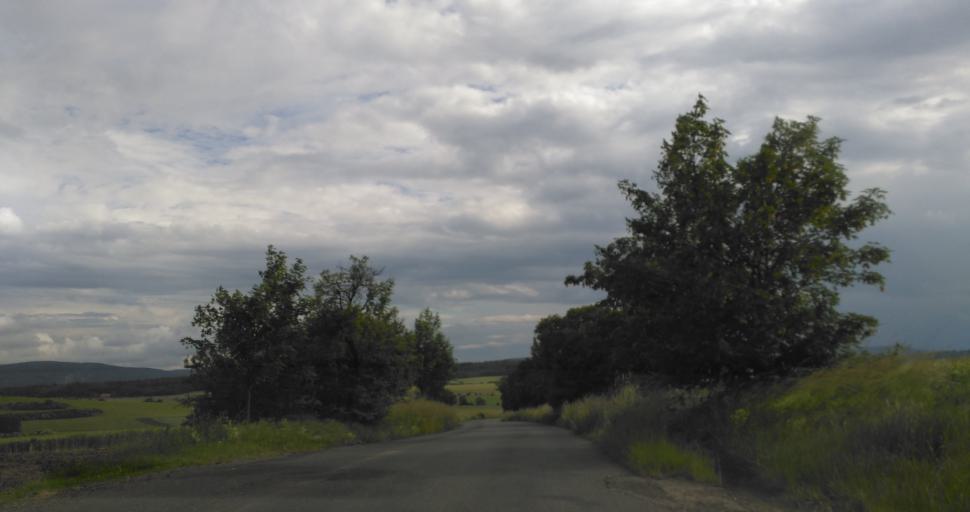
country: CZ
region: Central Bohemia
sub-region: Okres Beroun
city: Kraluv Dvur
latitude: 49.8914
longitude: 14.0748
